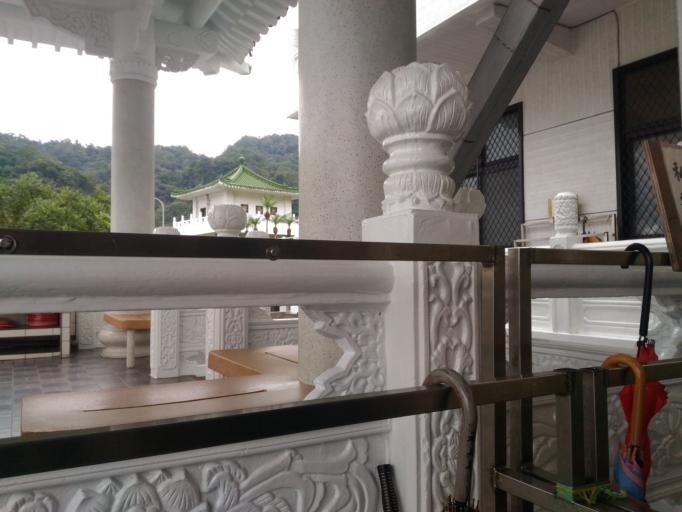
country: TW
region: Taipei
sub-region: Taipei
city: Banqiao
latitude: 24.9509
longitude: 121.4463
